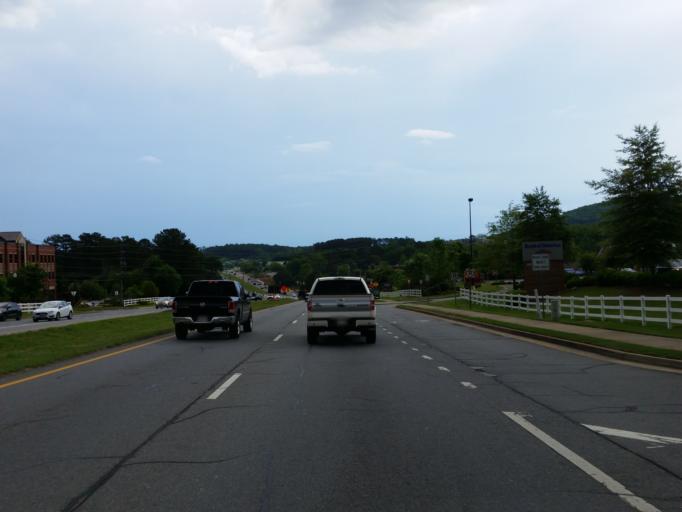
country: US
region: Georgia
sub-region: Cherokee County
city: Woodstock
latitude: 34.0874
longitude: -84.4826
